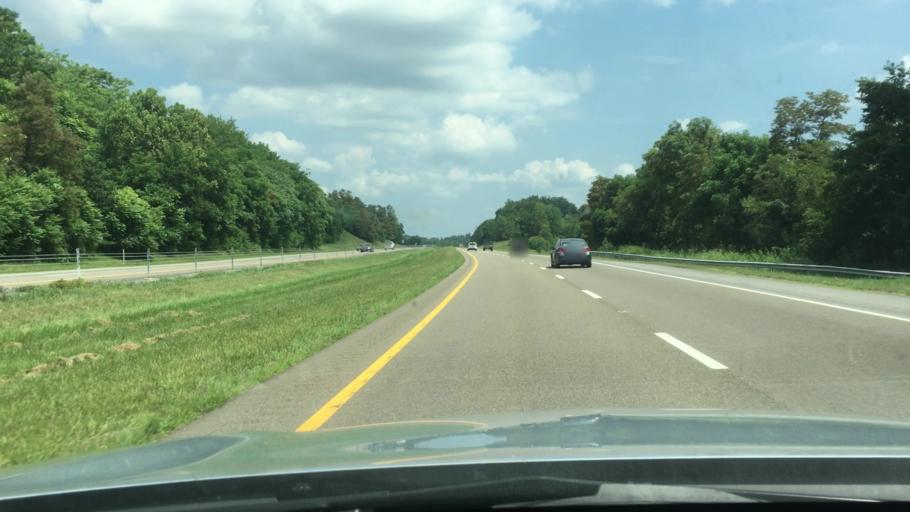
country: US
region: Tennessee
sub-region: Carter County
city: Pine Crest
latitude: 36.2557
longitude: -82.3229
